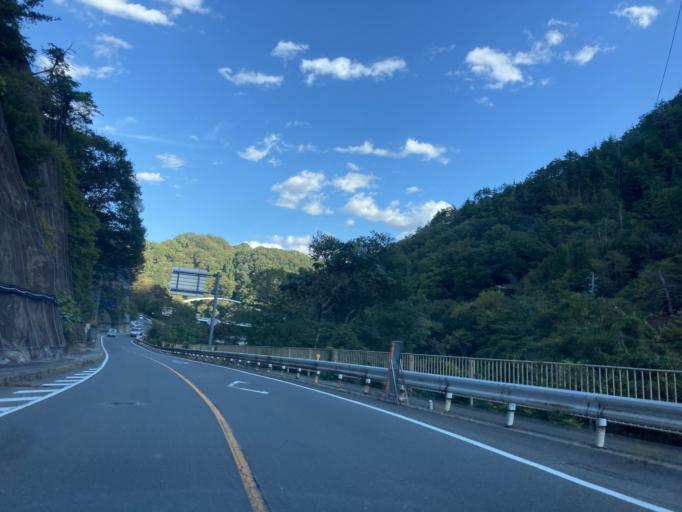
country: JP
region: Nagano
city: Omachi
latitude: 36.4652
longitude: 137.9544
